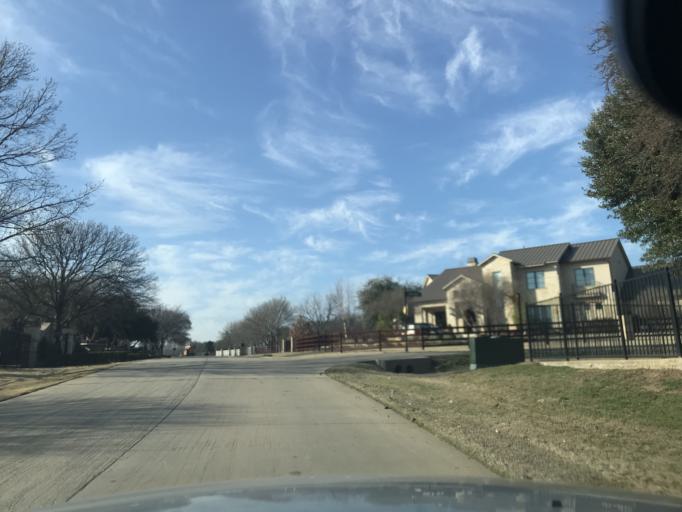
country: US
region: Texas
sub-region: Collin County
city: Frisco
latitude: 33.0964
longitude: -96.8312
